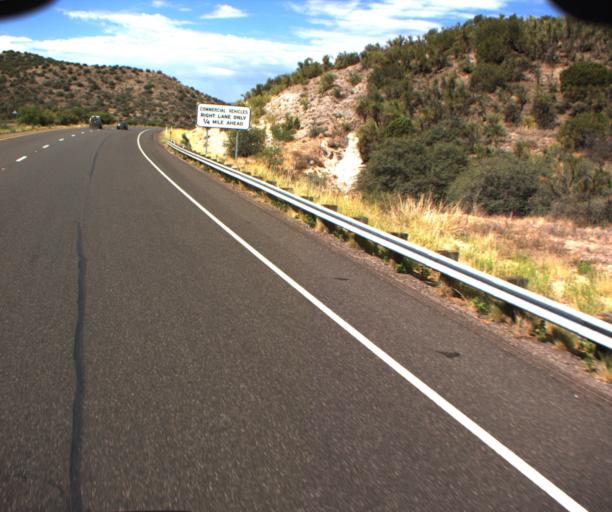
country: US
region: Arizona
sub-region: Yavapai County
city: Lake Montezuma
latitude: 34.6867
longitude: -111.7449
